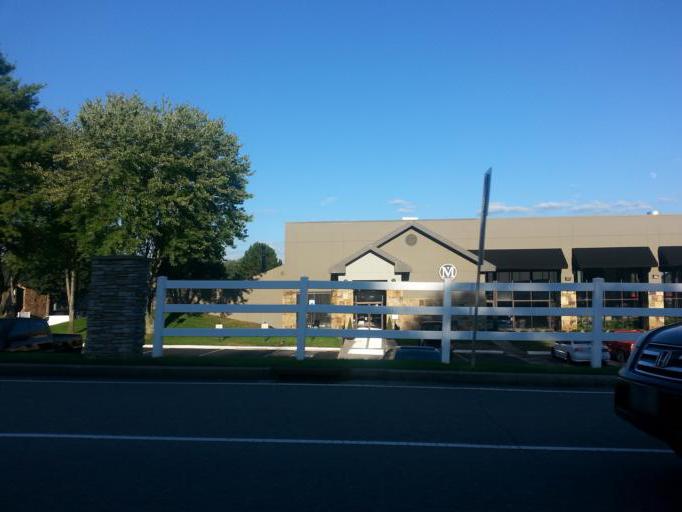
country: US
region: Tennessee
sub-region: Knox County
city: Farragut
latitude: 35.9354
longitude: -84.0949
